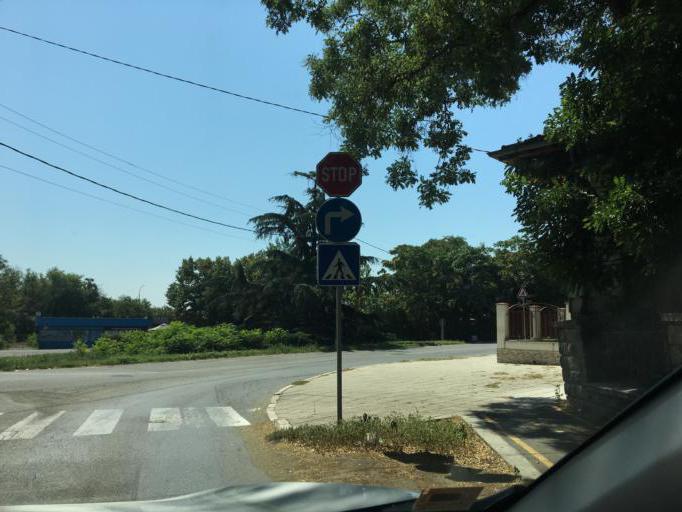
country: BG
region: Burgas
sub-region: Obshtina Kameno
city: Kameno
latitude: 42.6110
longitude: 27.3928
